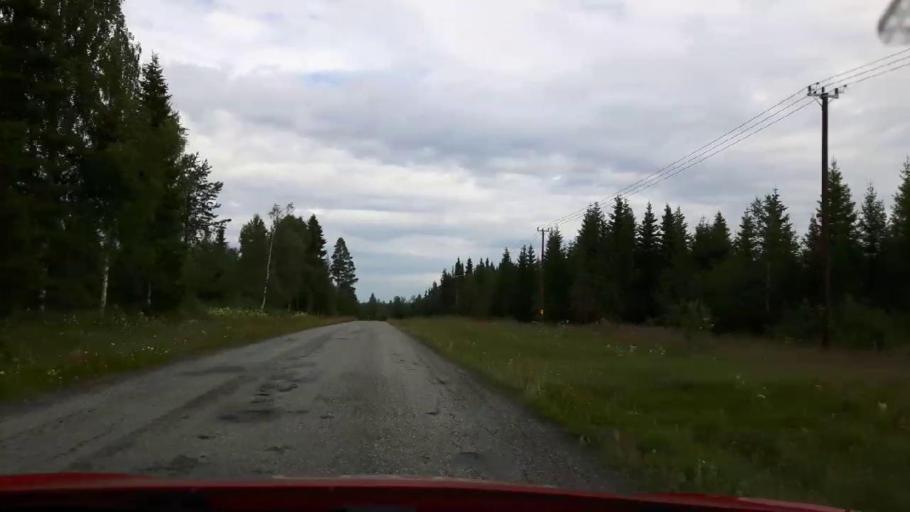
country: SE
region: Jaemtland
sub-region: Stroemsunds Kommun
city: Stroemsund
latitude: 63.5336
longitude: 15.3543
